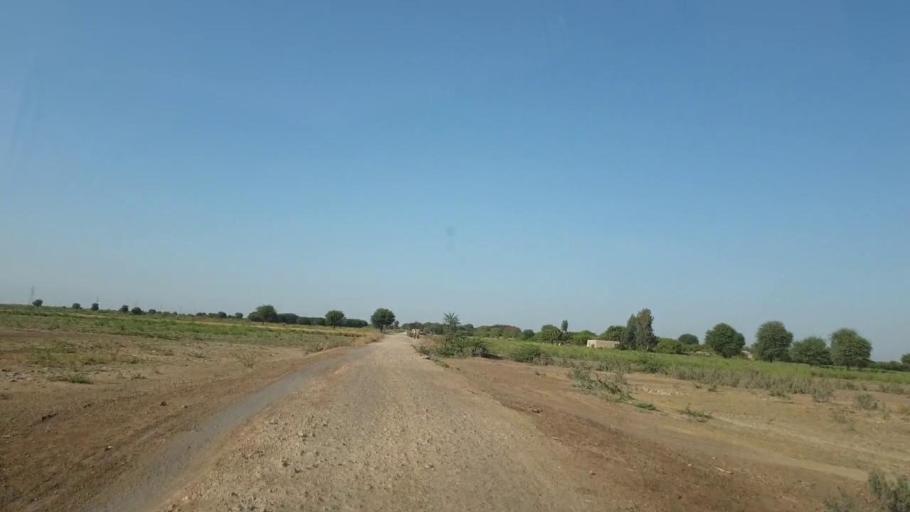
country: PK
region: Sindh
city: Kunri
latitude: 25.0453
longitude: 69.4420
